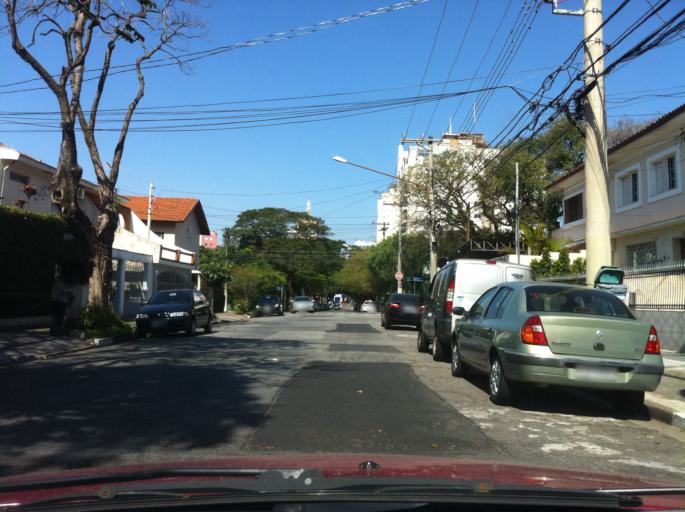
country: BR
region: Sao Paulo
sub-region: Diadema
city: Diadema
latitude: -23.6255
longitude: -46.6441
